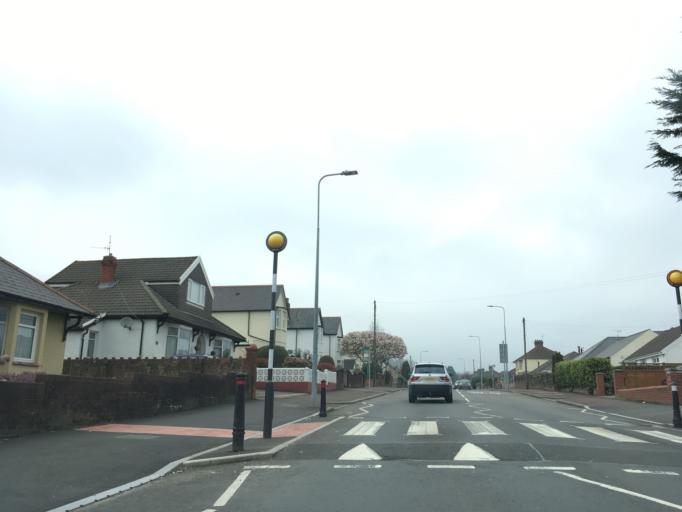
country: GB
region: Wales
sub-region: Cardiff
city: Cardiff
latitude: 51.5216
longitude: -3.1797
